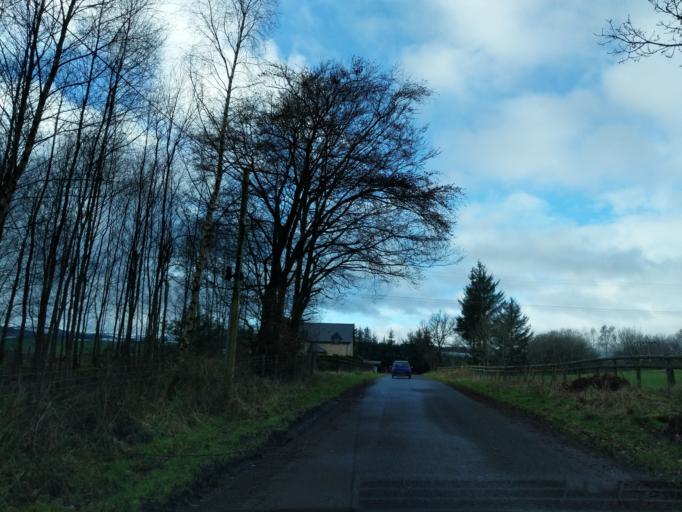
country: GB
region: Scotland
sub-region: Dumfries and Galloway
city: Moffat
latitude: 55.3204
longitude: -3.4277
